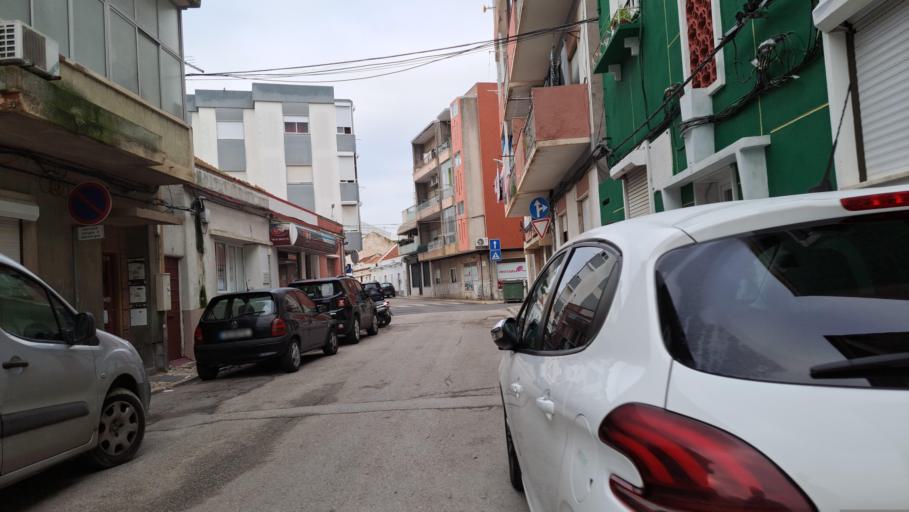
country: PT
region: Setubal
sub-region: Moita
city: Alhos Vedros
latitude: 38.6585
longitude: -9.0456
